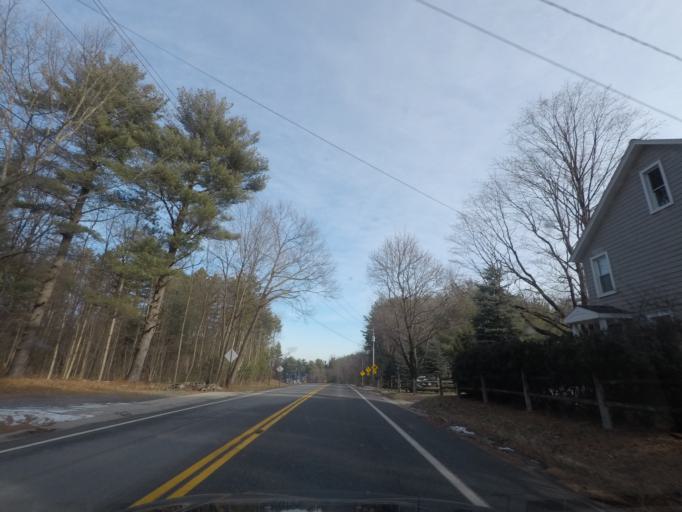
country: US
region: New York
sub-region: Saratoga County
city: Country Knolls
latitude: 42.9845
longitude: -73.7625
